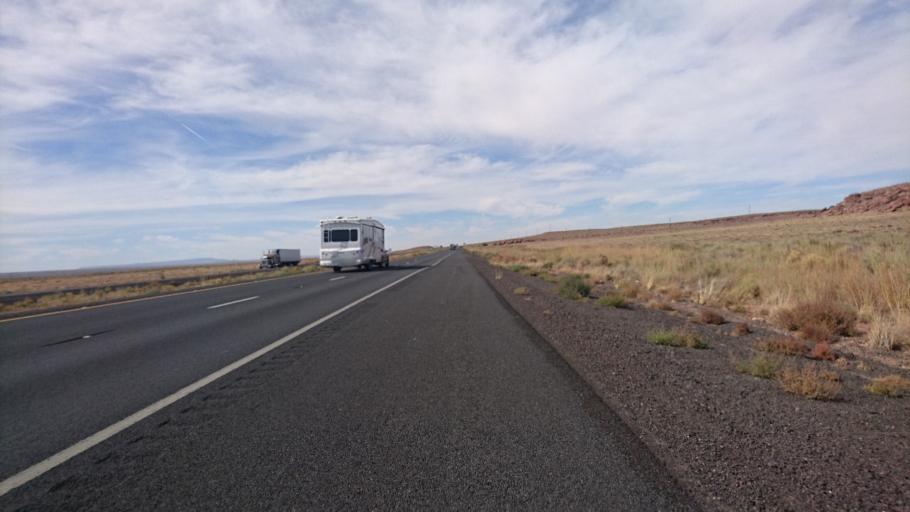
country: US
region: Arizona
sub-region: Navajo County
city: Joseph City
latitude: 34.9723
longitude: -110.4880
